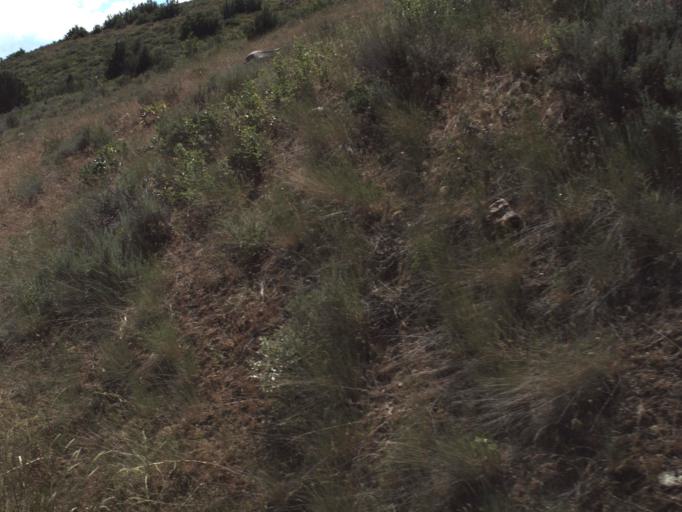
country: US
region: Utah
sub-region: Weber County
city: Wolf Creek
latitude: 41.3587
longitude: -111.5934
